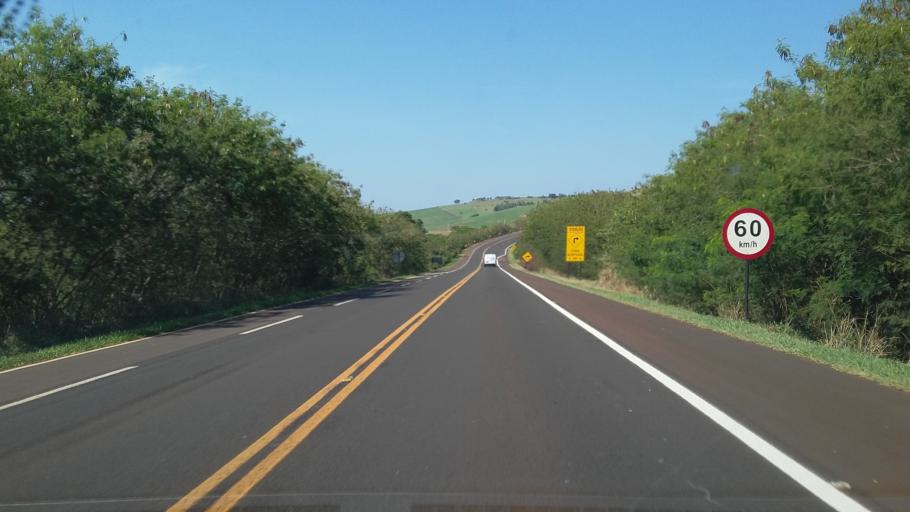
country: BR
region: Parana
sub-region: Bandeirantes
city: Bandeirantes
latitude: -23.1368
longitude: -50.3793
